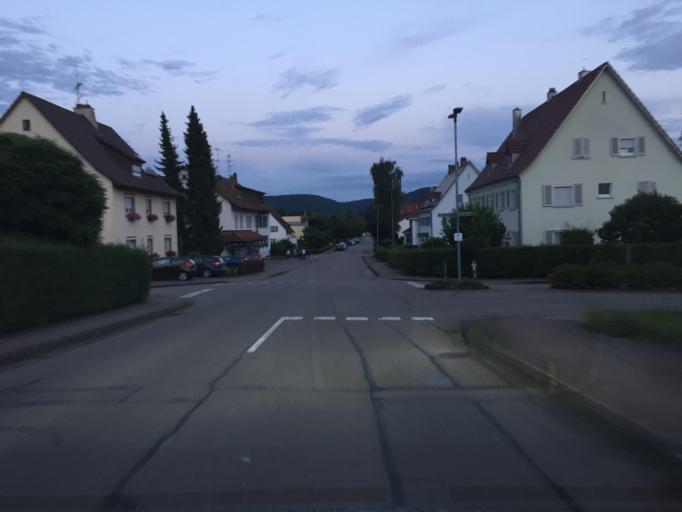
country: CH
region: Schaffhausen
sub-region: Bezirk Unterklettgau
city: Wilchingen
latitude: 47.6600
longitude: 8.4260
